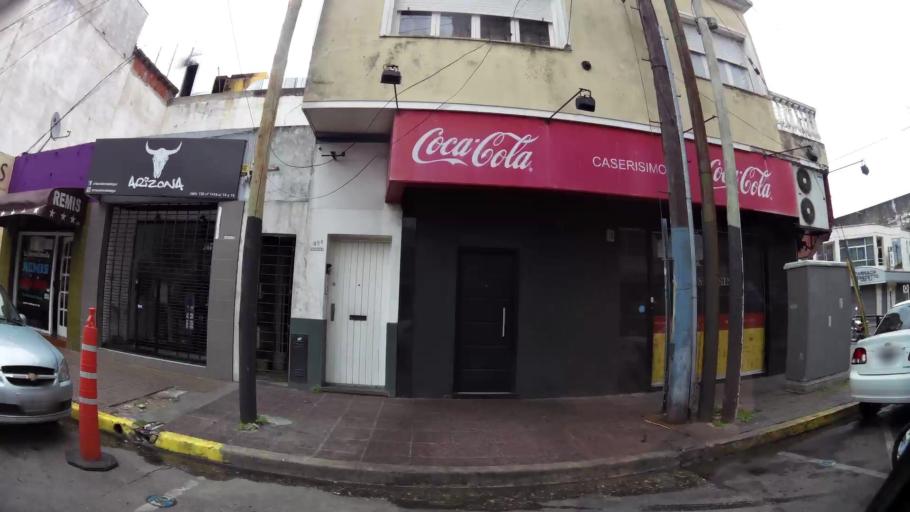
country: AR
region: Buenos Aires
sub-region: Partido de Quilmes
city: Quilmes
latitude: -34.7608
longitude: -58.2070
